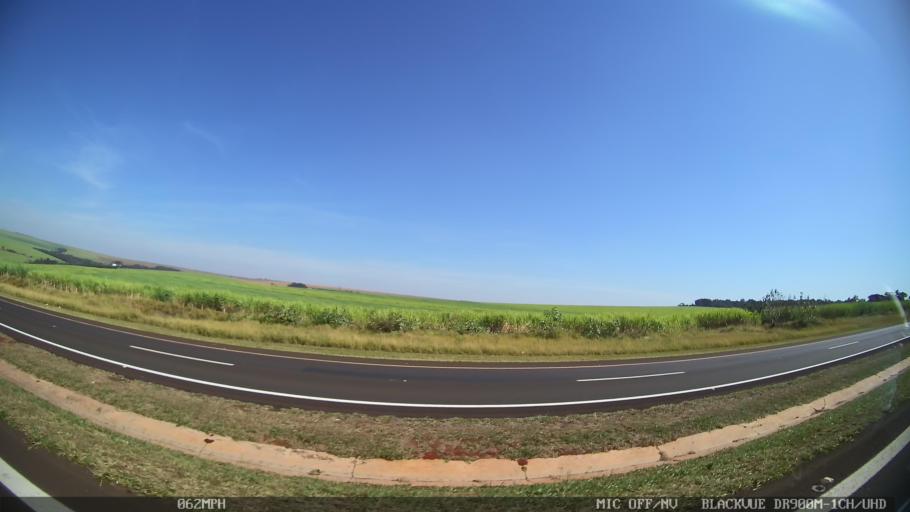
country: BR
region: Sao Paulo
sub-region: Ribeirao Preto
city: Ribeirao Preto
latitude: -21.1862
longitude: -47.8890
